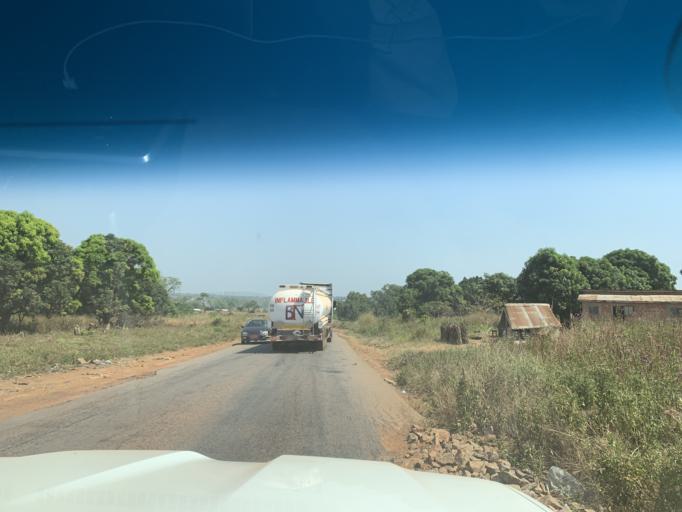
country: GN
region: Kindia
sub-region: Kindia
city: Kindia
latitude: 9.9999
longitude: -12.7080
